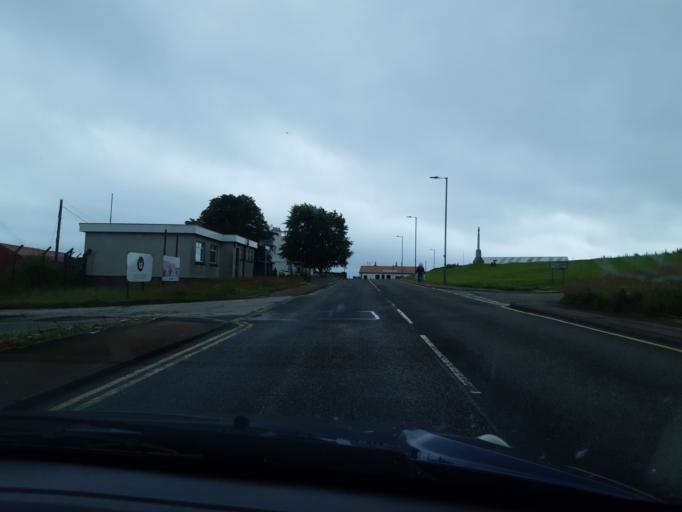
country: GB
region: Scotland
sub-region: Argyll and Bute
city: Ardrishaig
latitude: 56.0143
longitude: -5.4473
